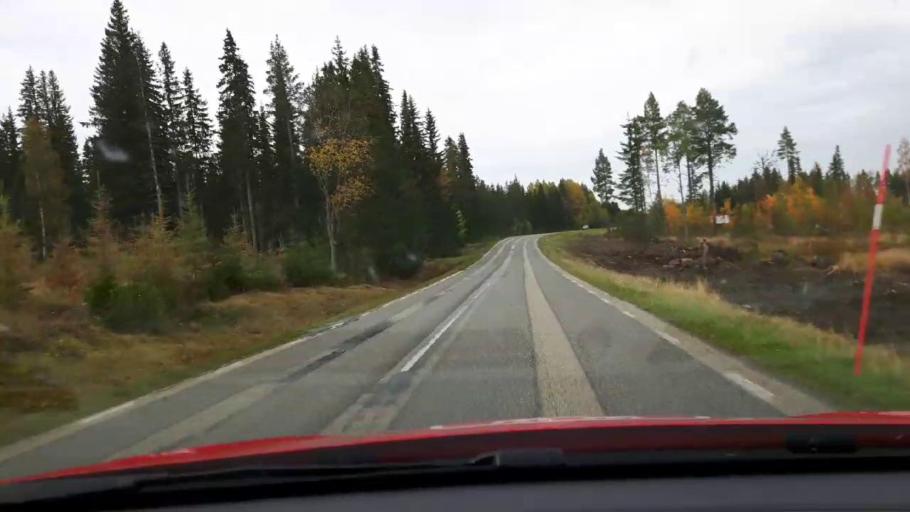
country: SE
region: Jaemtland
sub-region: Bergs Kommun
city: Hoverberg
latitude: 62.8214
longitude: 14.3951
